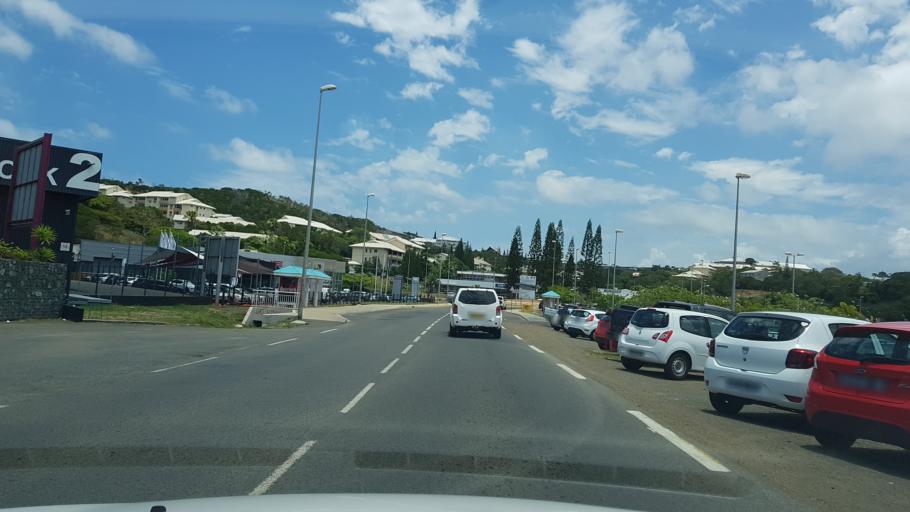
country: NC
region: South Province
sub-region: Noumea
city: Noumea
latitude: -22.2615
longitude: 166.4710
